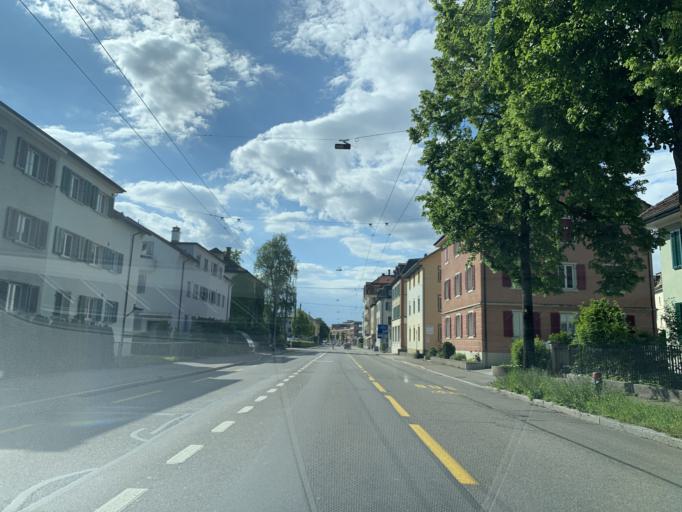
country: CH
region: Zurich
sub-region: Bezirk Winterthur
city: Mattenbach (Kreis 7) / Deutweg
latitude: 47.4924
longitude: 8.7445
